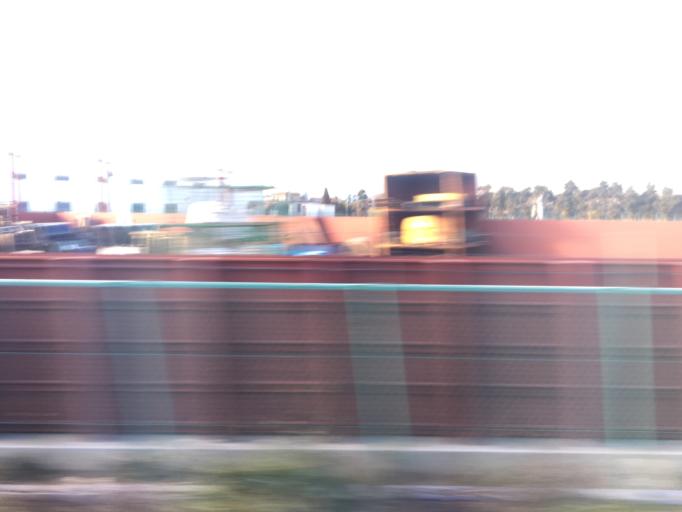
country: JP
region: Gunma
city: Omamacho-omama
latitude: 36.3704
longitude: 139.2573
